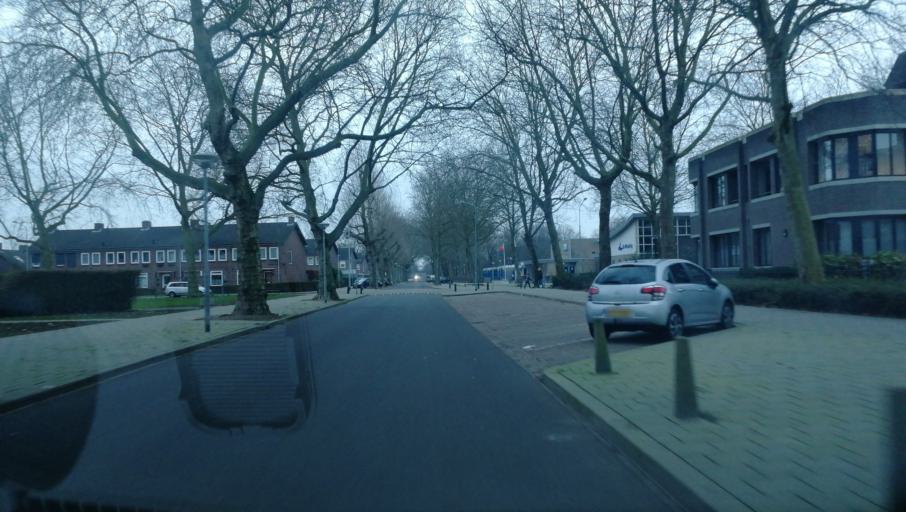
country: NL
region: Limburg
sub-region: Gemeente Venlo
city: Tegelen
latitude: 51.3685
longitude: 6.1377
